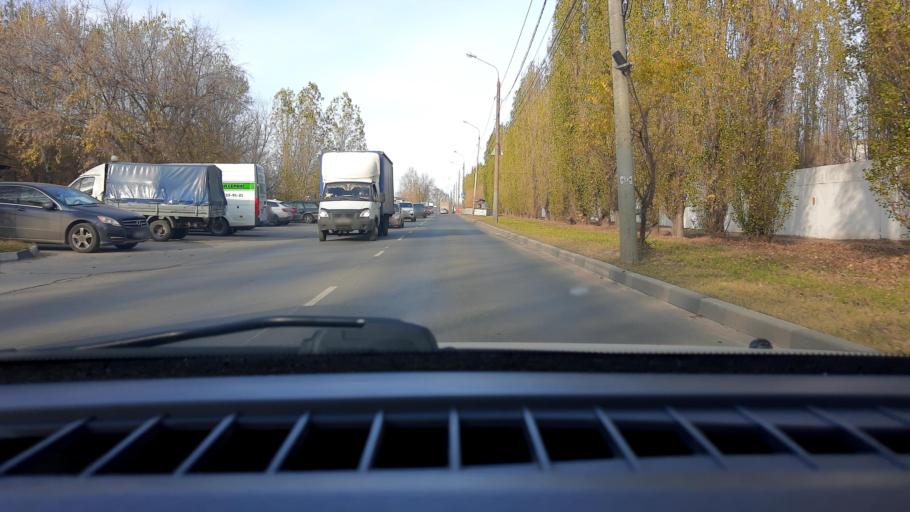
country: RU
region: Nizjnij Novgorod
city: Gorbatovka
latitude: 56.3461
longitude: 43.8061
